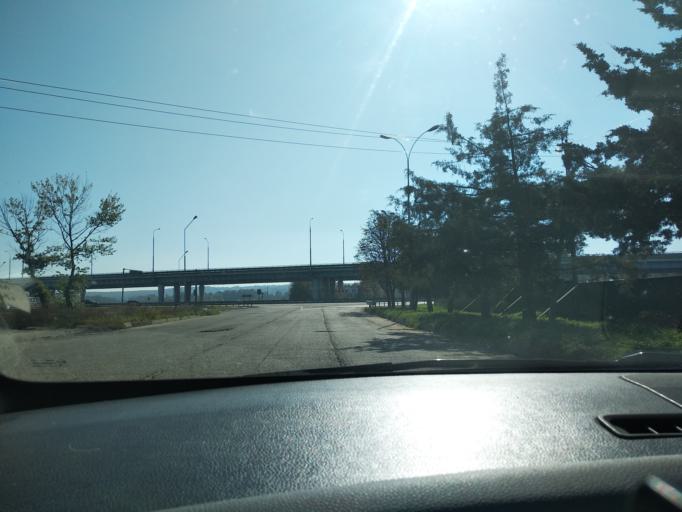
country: RU
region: Krasnodarskiy
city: Goryachiy Klyuch
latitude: 44.6459
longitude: 39.1289
